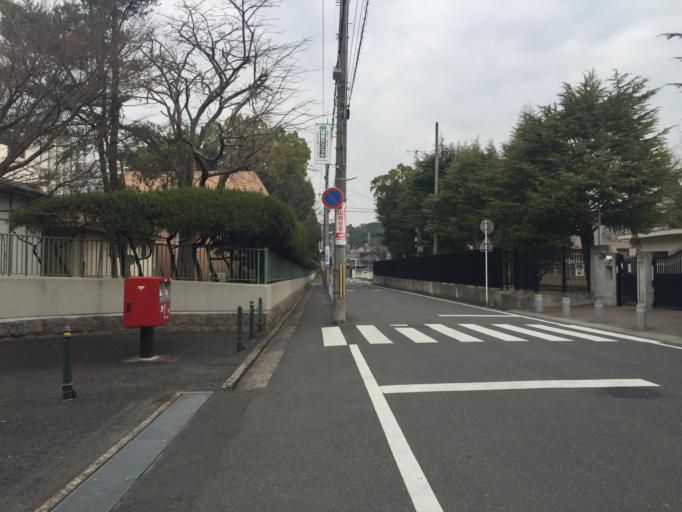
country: JP
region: Nara
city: Nara-shi
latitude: 34.6879
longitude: 135.8297
